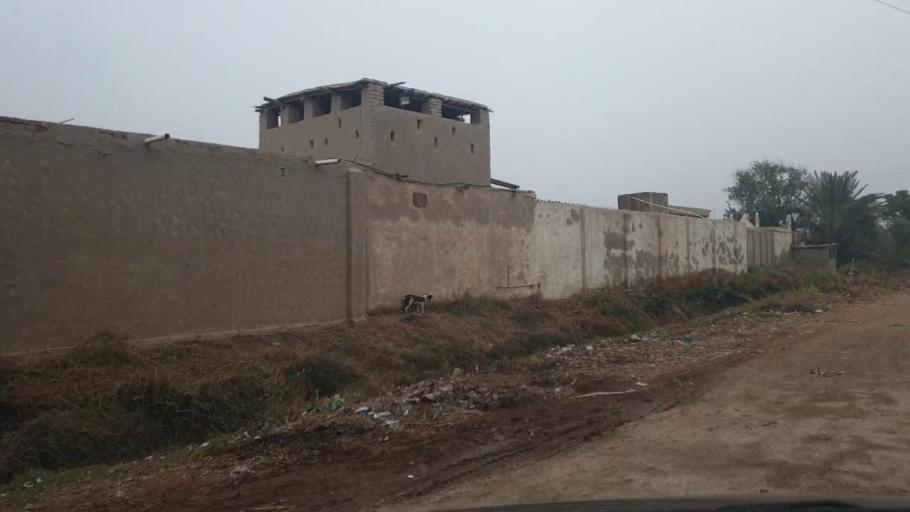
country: PK
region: Sindh
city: Tando Adam
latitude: 25.8056
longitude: 68.6846
